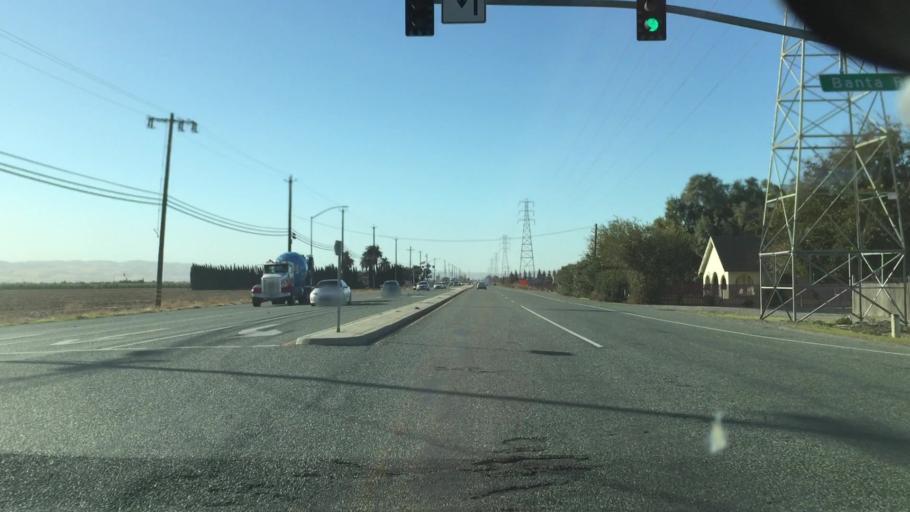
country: US
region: California
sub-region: San Joaquin County
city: Tracy
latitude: 37.7398
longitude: -121.3800
